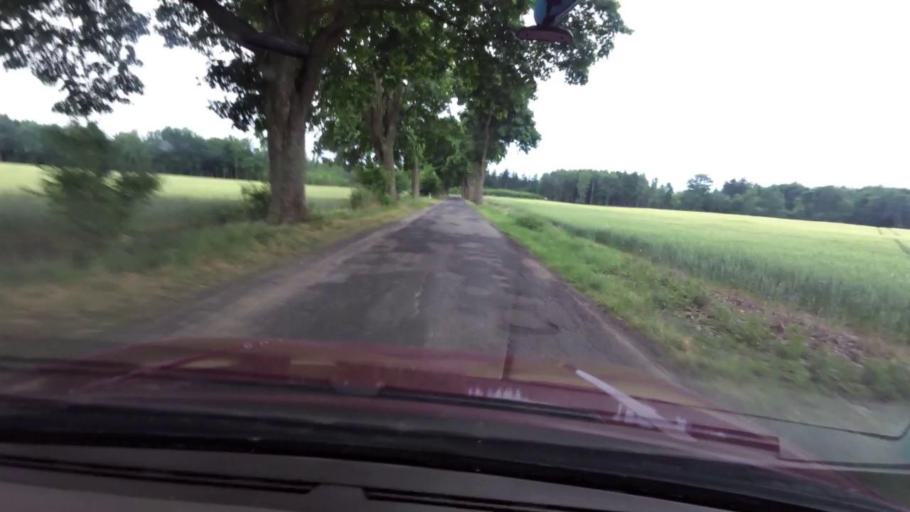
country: PL
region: Pomeranian Voivodeship
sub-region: Powiat slupski
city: Kepice
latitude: 54.1819
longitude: 16.7912
